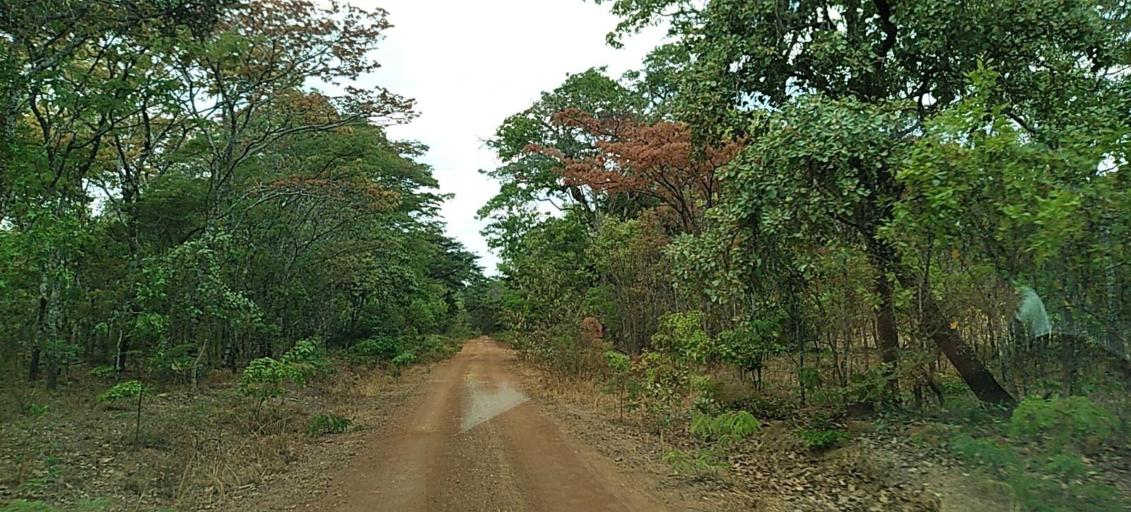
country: ZM
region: Copperbelt
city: Chililabombwe
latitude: -12.4504
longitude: 27.6148
